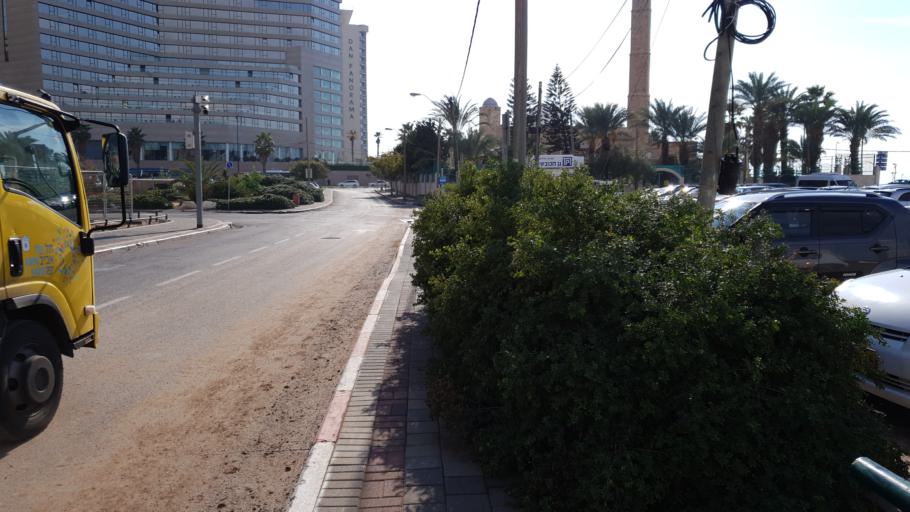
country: IL
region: Tel Aviv
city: Yafo
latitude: 32.0670
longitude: 34.7642
